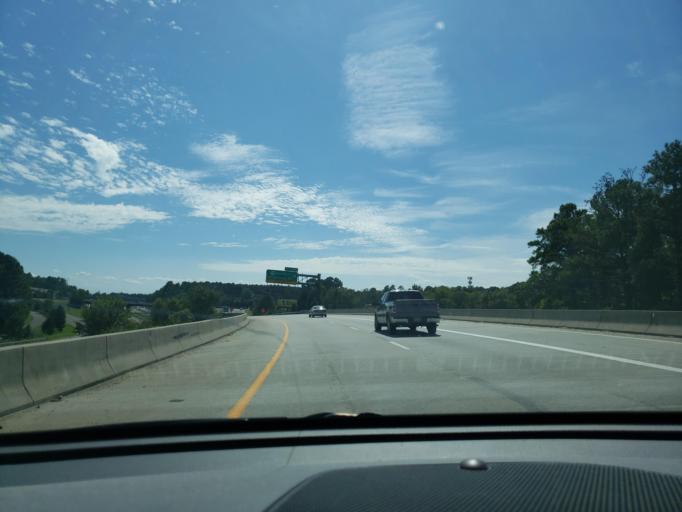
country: US
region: North Carolina
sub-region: Durham County
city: Durham
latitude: 36.0242
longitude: -78.9483
